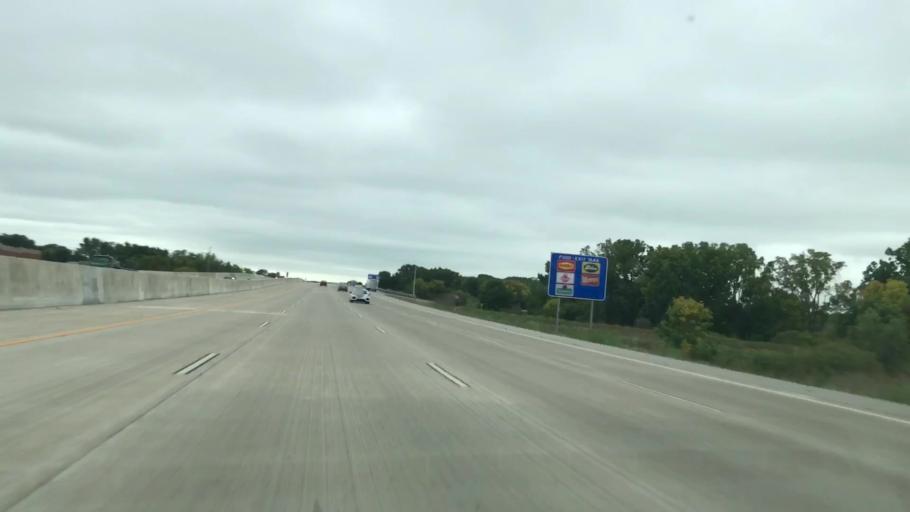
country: US
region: Wisconsin
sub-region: Brown County
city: Ashwaubenon
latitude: 44.4887
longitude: -88.0810
